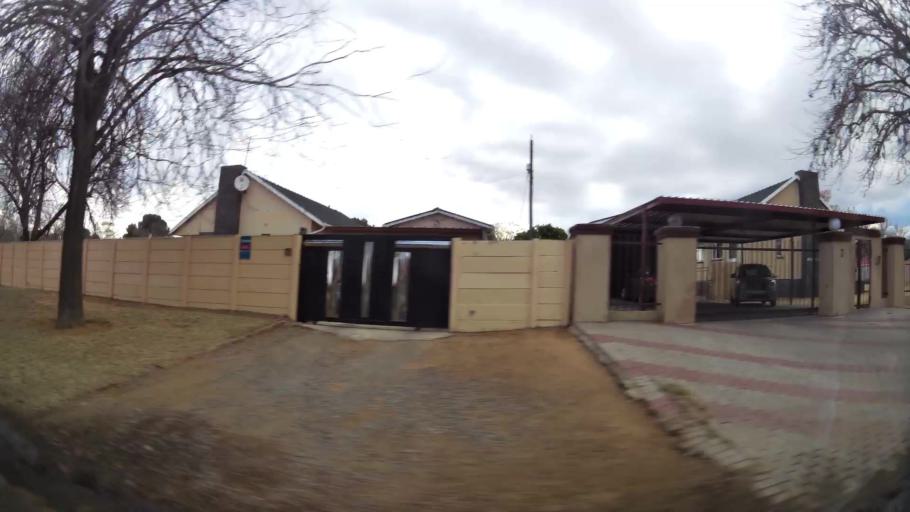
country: ZA
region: Orange Free State
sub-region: Lejweleputswa District Municipality
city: Welkom
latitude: -27.9757
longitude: 26.7001
